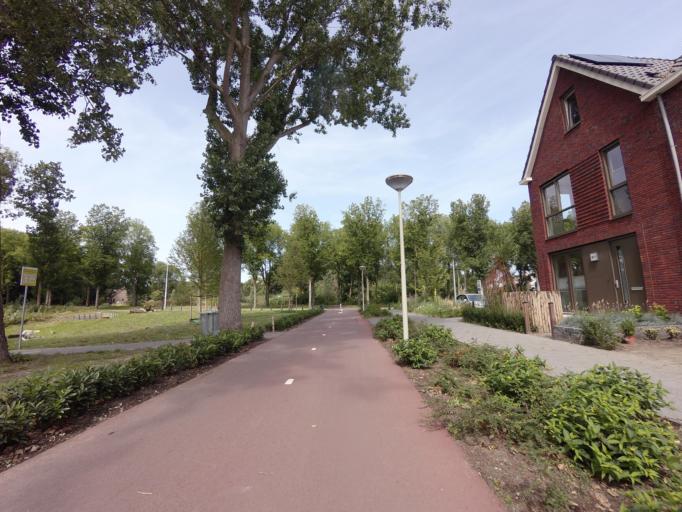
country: NL
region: South Holland
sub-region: Gemeente Westland
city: Kwintsheul
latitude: 52.0556
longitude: 4.2603
